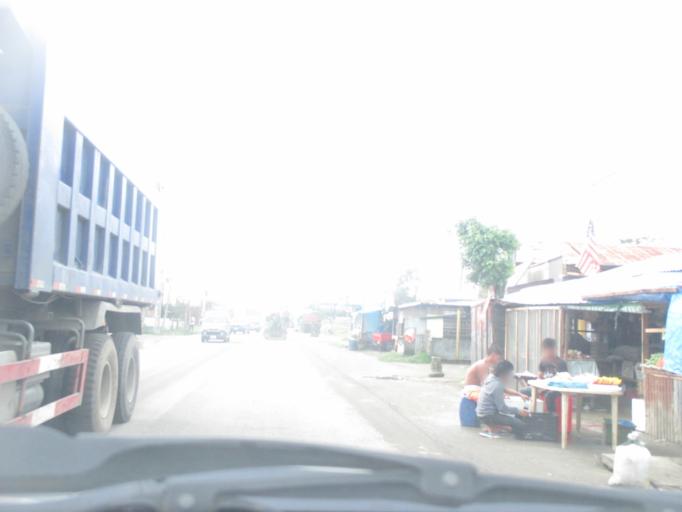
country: PH
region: Eastern Visayas
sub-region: Province of Leyte
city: Panalanoy
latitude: 11.2446
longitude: 124.9833
